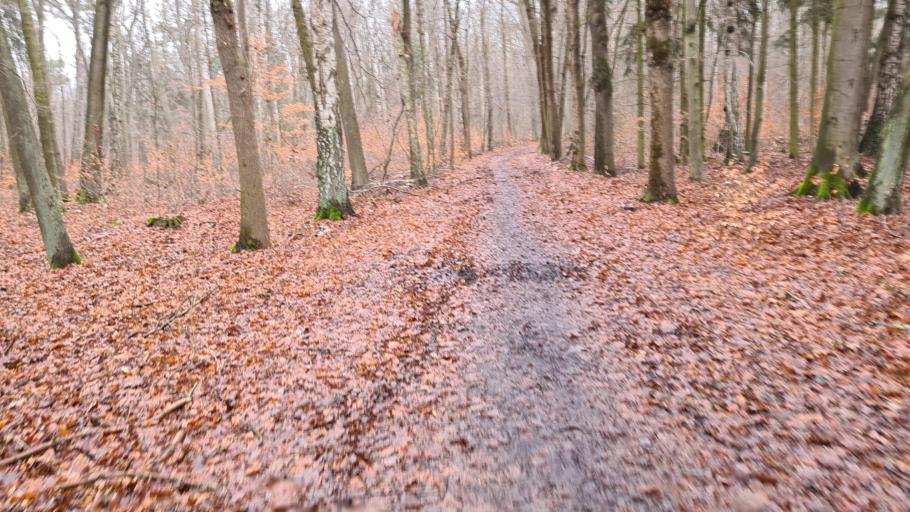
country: DE
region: Brandenburg
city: Finsterwalde
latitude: 51.6249
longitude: 13.6857
